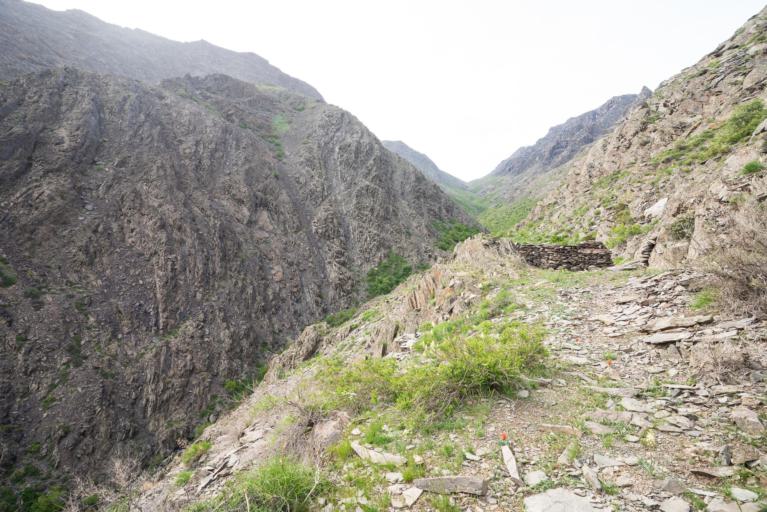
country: KZ
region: Ongtustik Qazaqstan
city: Kentau
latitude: 43.8456
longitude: 68.5036
